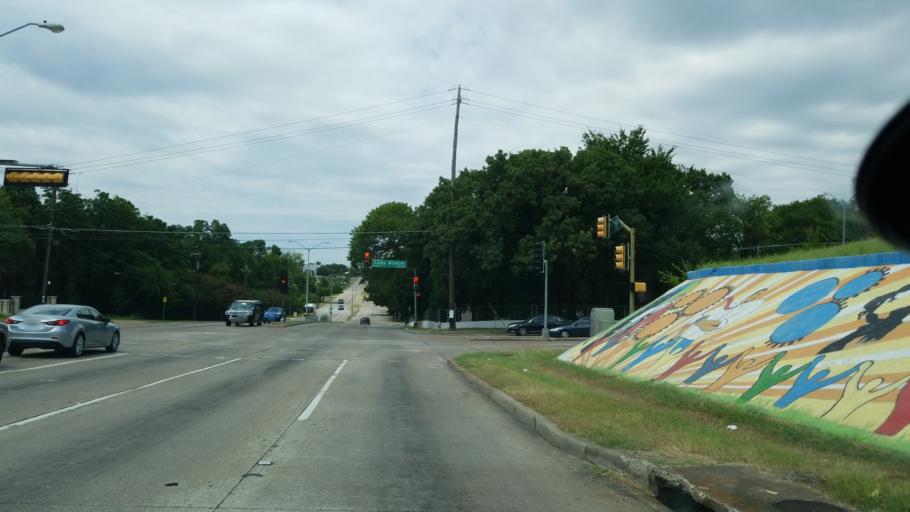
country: US
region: Texas
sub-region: Dallas County
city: Duncanville
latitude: 32.6617
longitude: -96.8570
